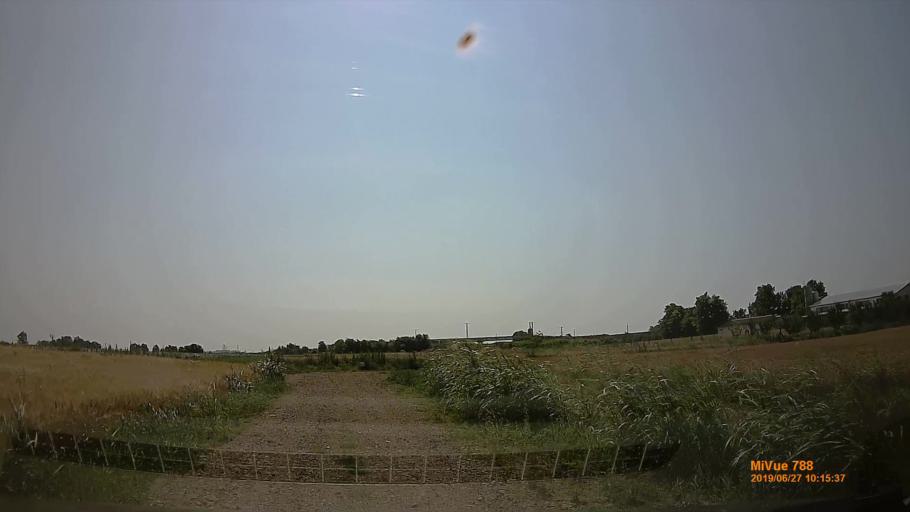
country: HU
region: Pest
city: Cegled
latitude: 47.1969
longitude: 19.8236
